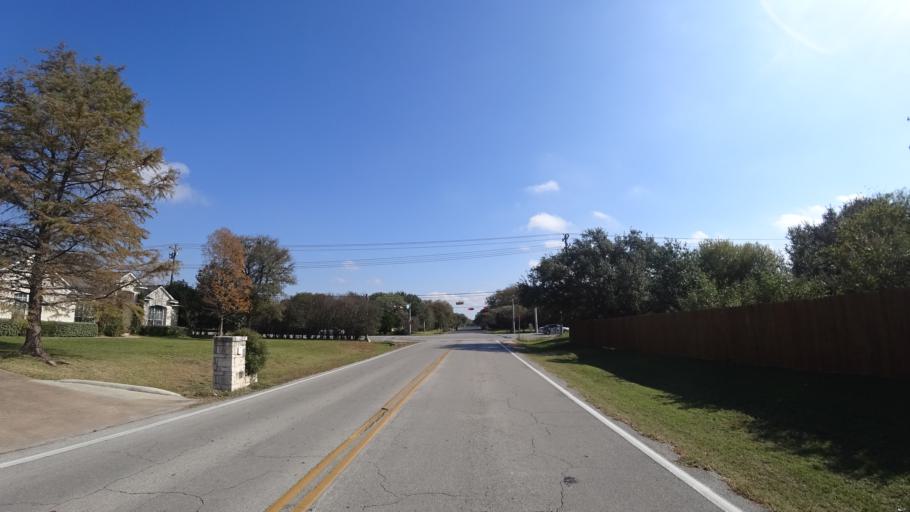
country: US
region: Texas
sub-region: Travis County
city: Shady Hollow
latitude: 30.1616
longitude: -97.8607
